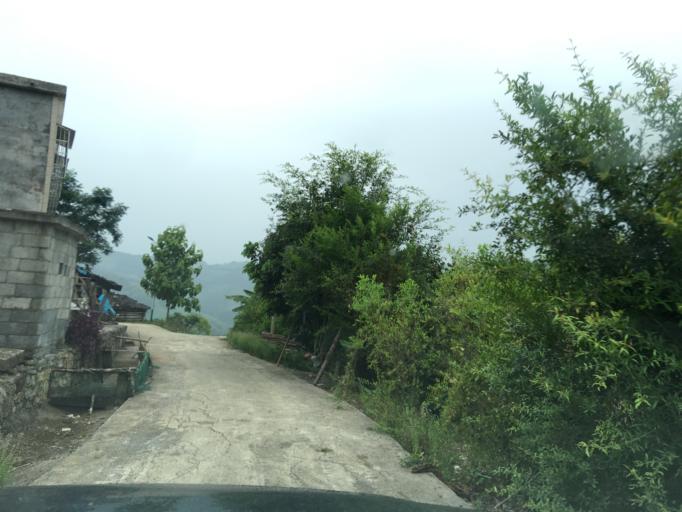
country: CN
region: Guangxi Zhuangzu Zizhiqu
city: Tongle
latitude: 25.0004
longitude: 105.9939
